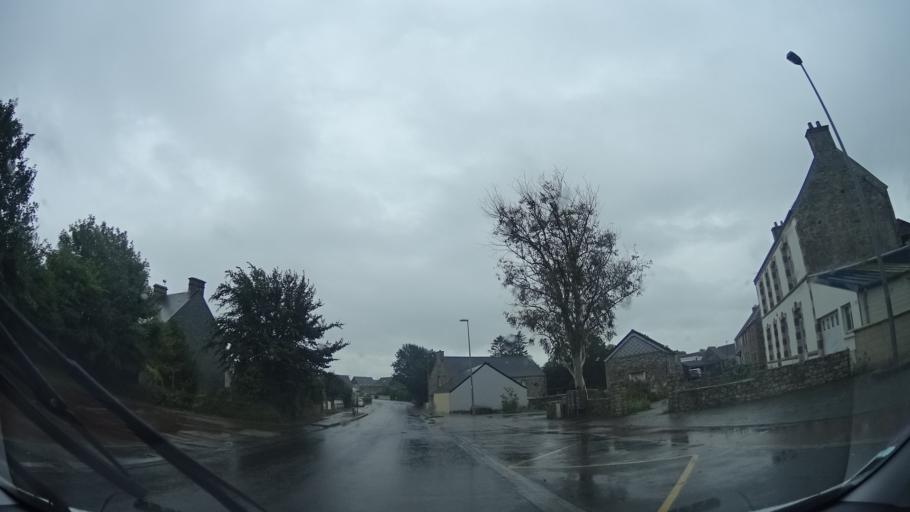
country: FR
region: Lower Normandy
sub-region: Departement de la Manche
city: Urville-Nacqueville
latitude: 49.5985
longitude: -1.7792
